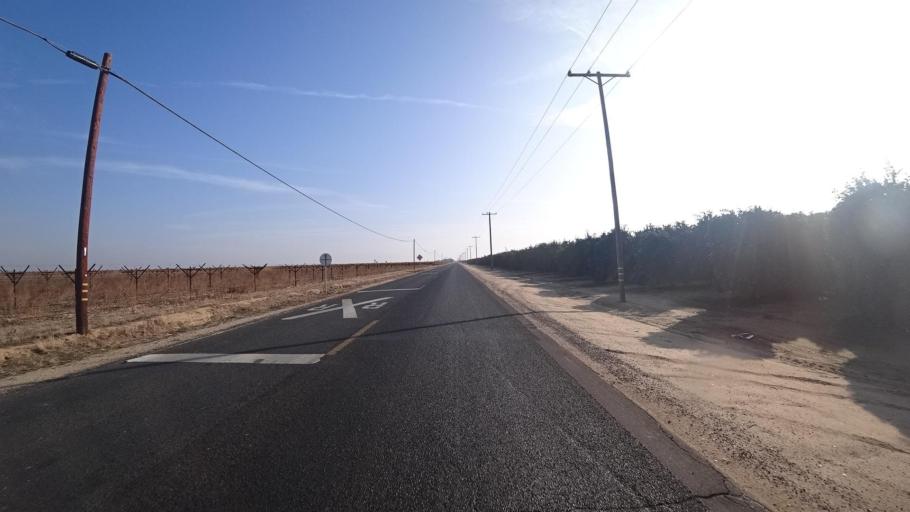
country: US
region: California
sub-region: Kern County
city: McFarland
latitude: 35.6746
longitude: -119.1847
